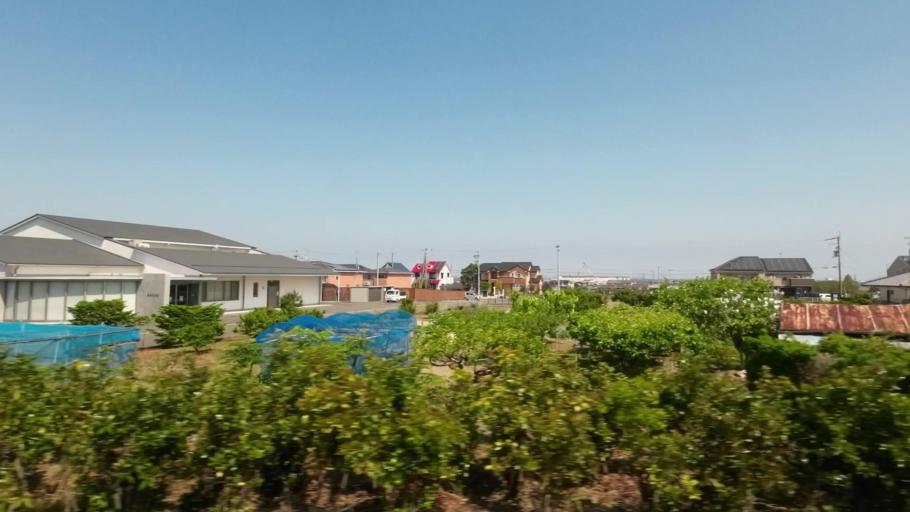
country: JP
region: Ehime
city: Kawanoecho
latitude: 33.9673
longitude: 133.4578
